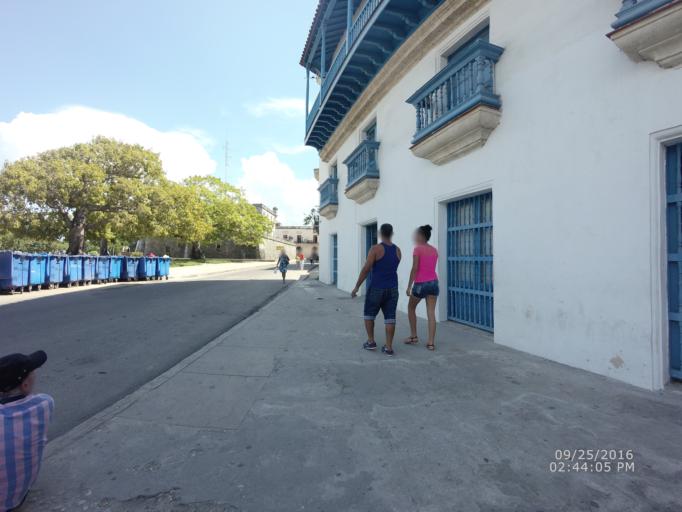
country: CU
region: La Habana
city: Centro Habana
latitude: 23.1430
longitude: -82.3539
